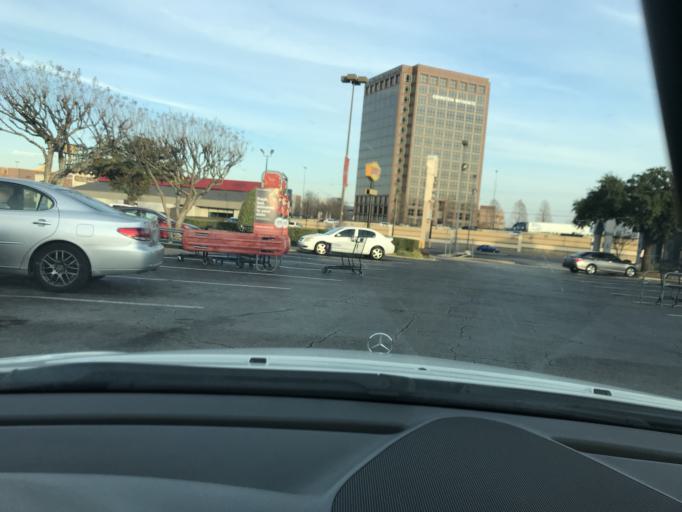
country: US
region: Texas
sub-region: Dallas County
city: University Park
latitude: 32.8887
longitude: -96.7716
